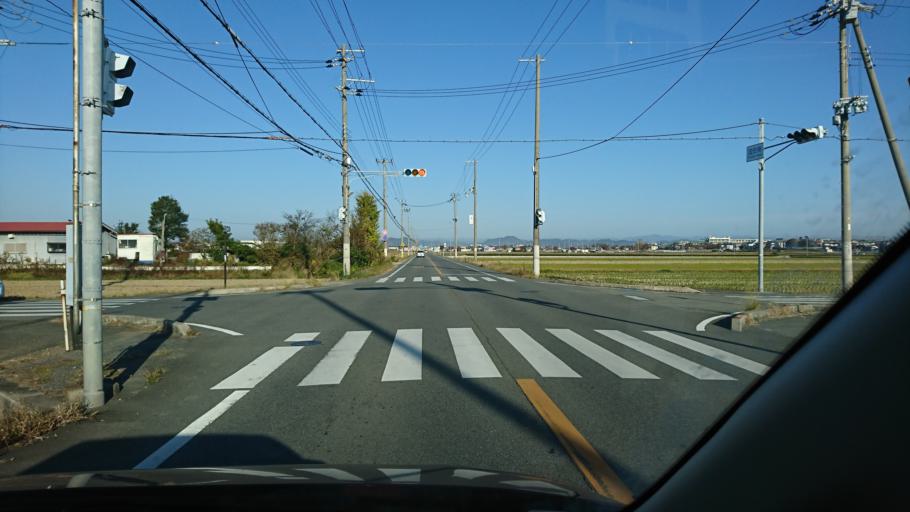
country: JP
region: Hyogo
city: Kakogawacho-honmachi
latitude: 34.7391
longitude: 134.9037
